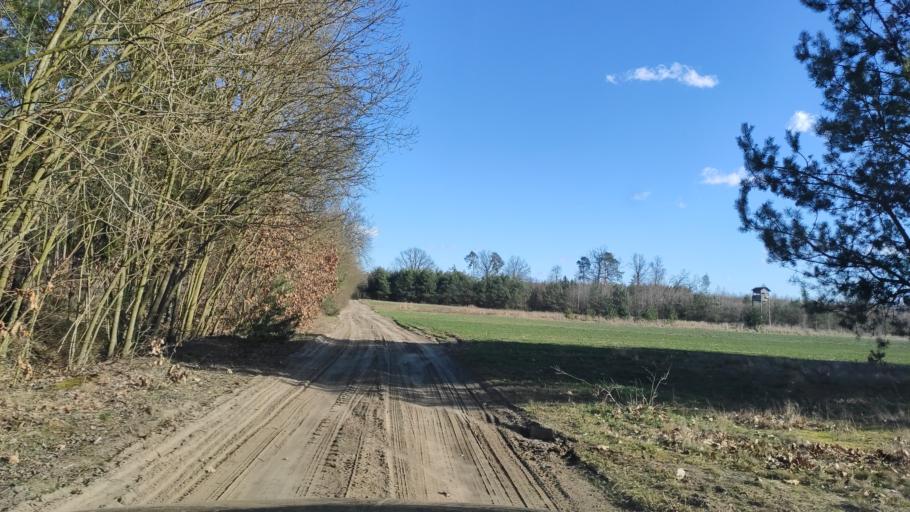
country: PL
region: Masovian Voivodeship
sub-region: Powiat radomski
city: Jedlnia-Letnisko
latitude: 51.4533
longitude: 21.2797
